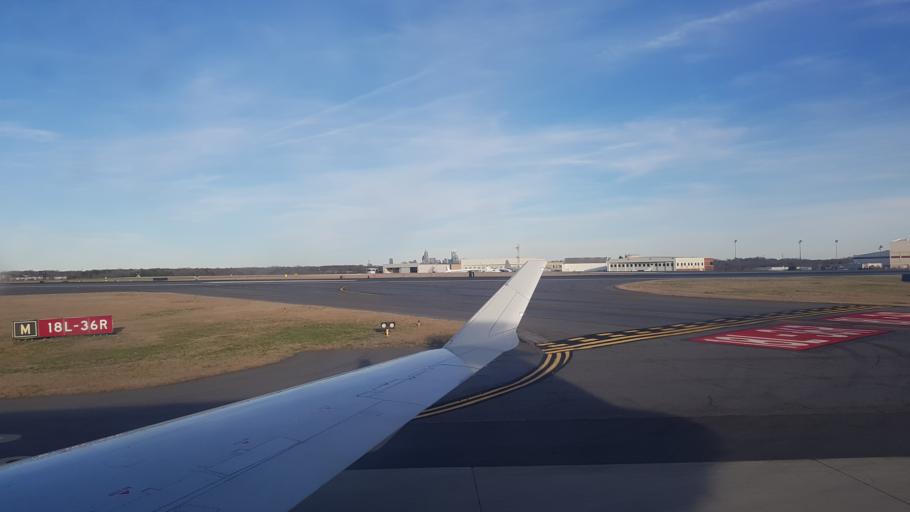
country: US
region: North Carolina
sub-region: Mecklenburg County
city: Charlotte
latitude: 35.2201
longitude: -80.9372
